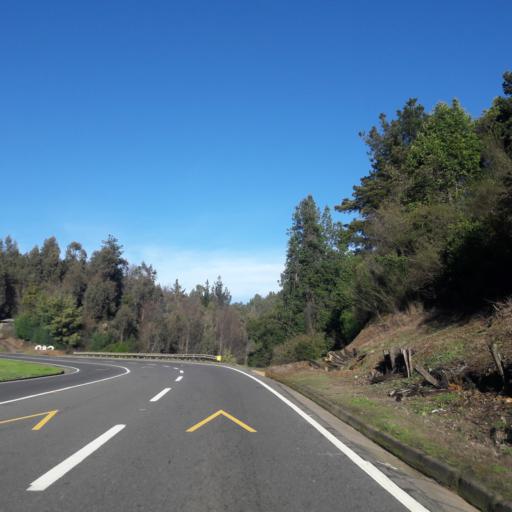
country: CL
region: Biobio
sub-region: Provincia de Biobio
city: La Laja
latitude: -37.2676
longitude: -72.9618
